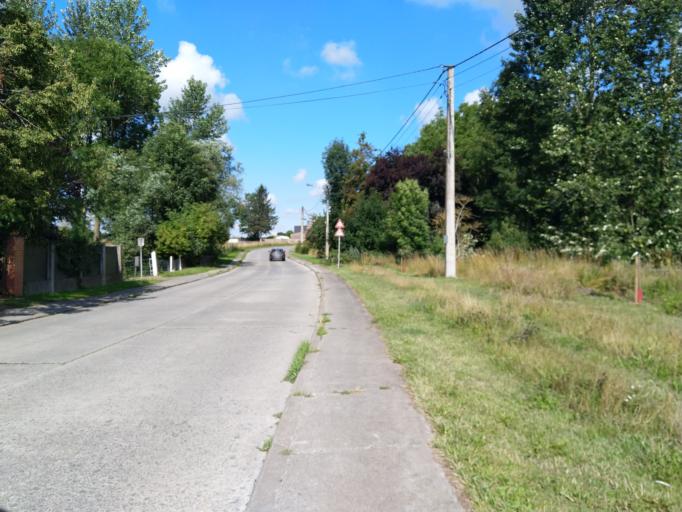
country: BE
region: Wallonia
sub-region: Province du Hainaut
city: Chievres
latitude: 50.5880
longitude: 3.7865
